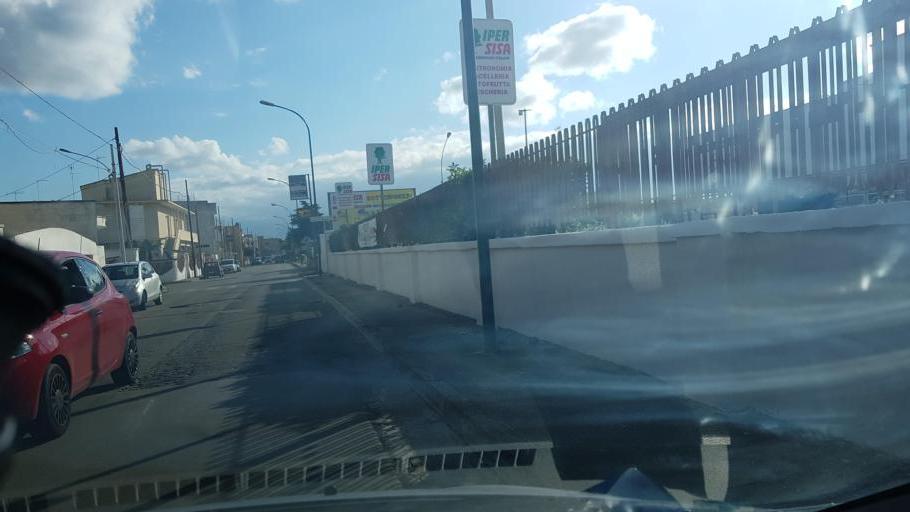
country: IT
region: Apulia
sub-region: Provincia di Lecce
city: Squinzano
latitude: 40.4355
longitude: 18.0318
